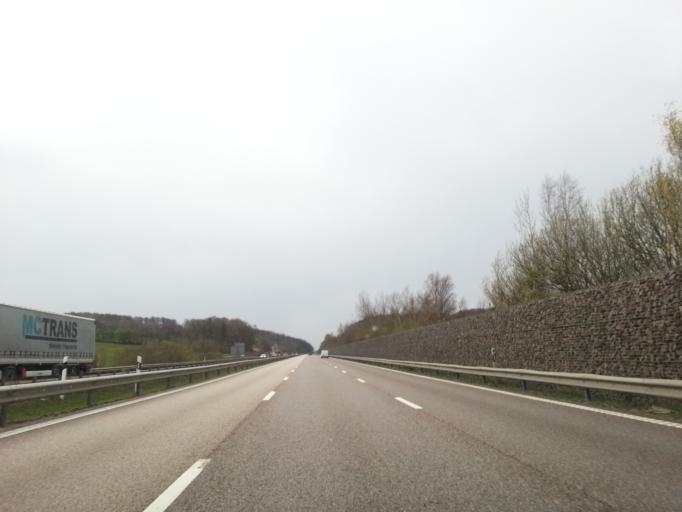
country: SE
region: Skane
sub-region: Bastads Kommun
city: Bastad
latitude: 56.4213
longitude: 12.9495
